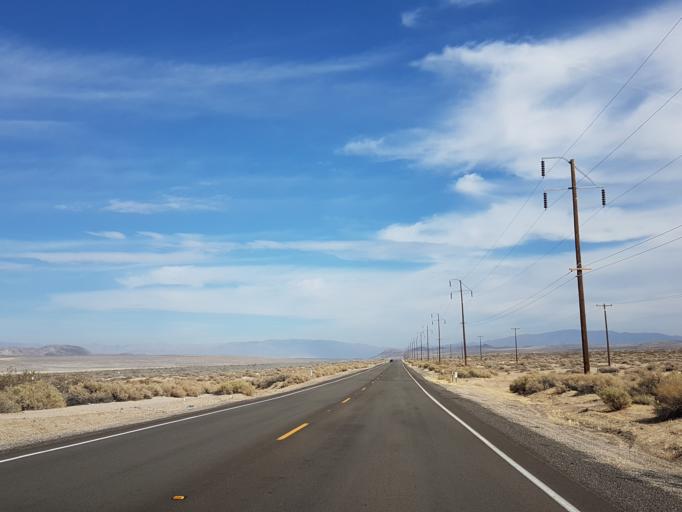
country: US
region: California
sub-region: Kern County
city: Ridgecrest
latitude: 35.6448
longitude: -117.5296
